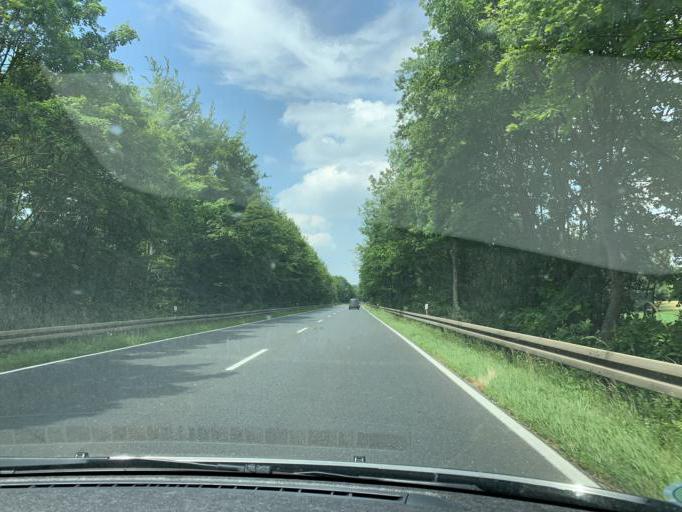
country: DE
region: North Rhine-Westphalia
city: Siersdorf
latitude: 50.8593
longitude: 6.2283
